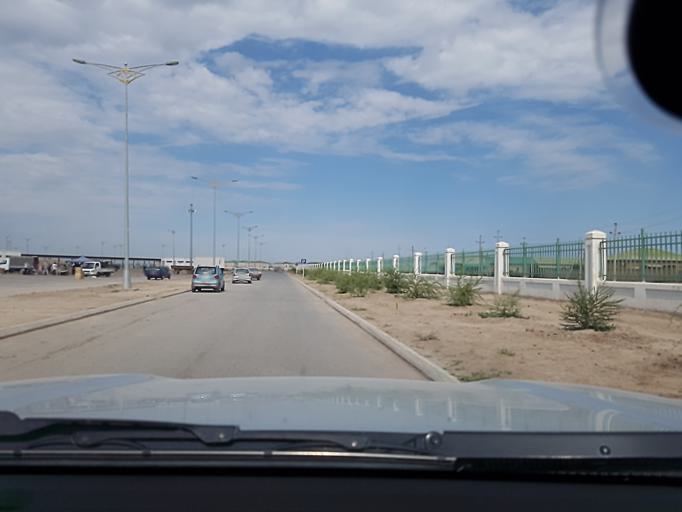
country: TM
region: Dasoguz
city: Dasoguz
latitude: 41.8804
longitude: 59.9526
